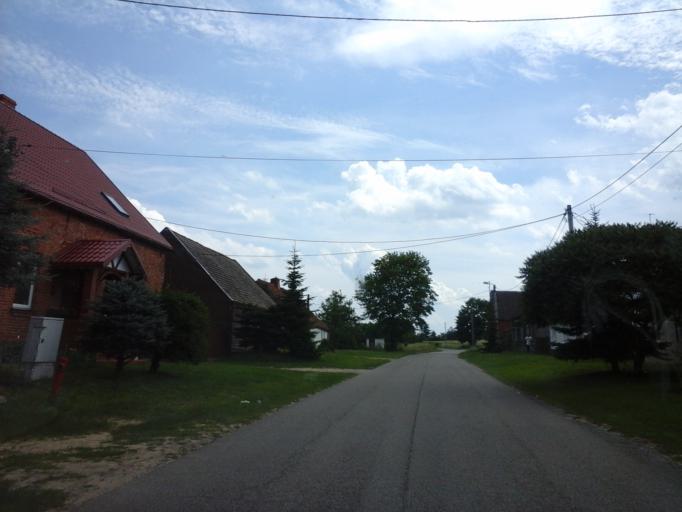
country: PL
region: West Pomeranian Voivodeship
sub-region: Powiat choszczenski
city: Bierzwnik
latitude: 53.0410
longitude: 15.6465
